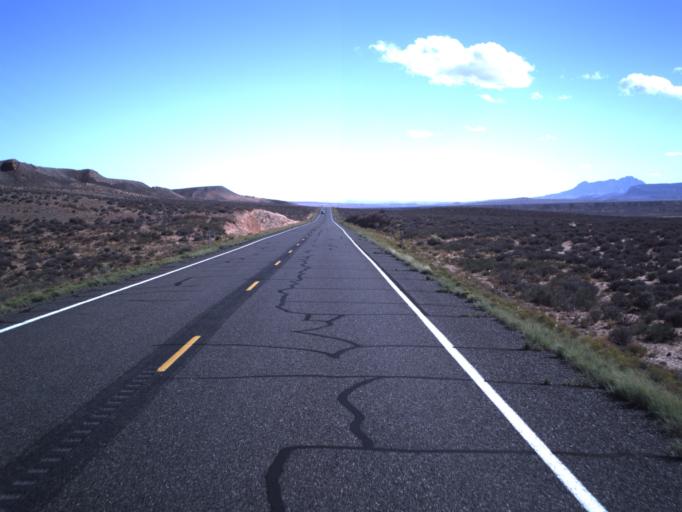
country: US
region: Utah
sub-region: Wayne County
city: Loa
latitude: 38.0950
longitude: -110.6204
